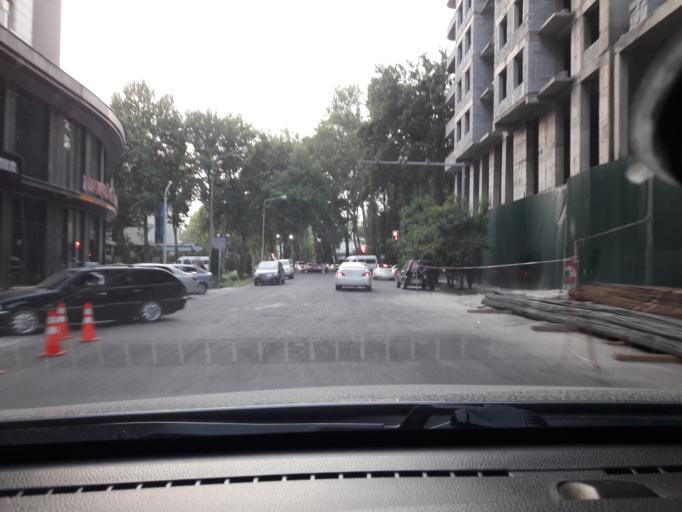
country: TJ
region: Dushanbe
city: Dushanbe
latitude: 38.5685
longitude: 68.7864
